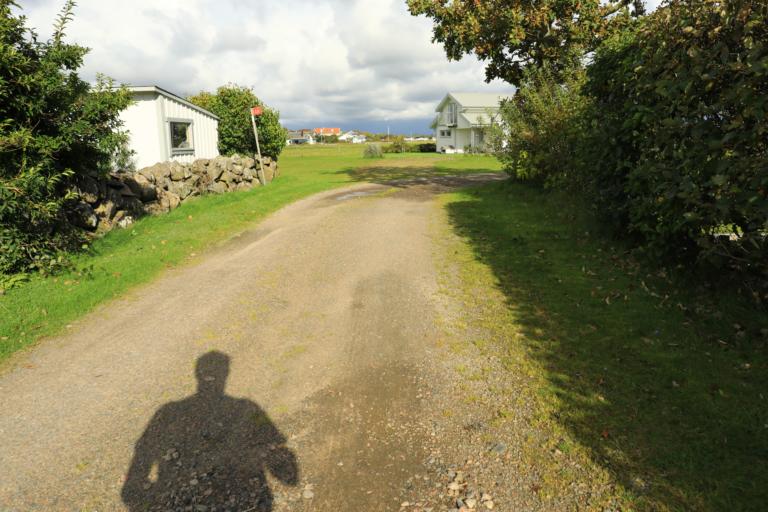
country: SE
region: Halland
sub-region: Varbergs Kommun
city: Traslovslage
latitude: 57.0680
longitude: 12.2611
